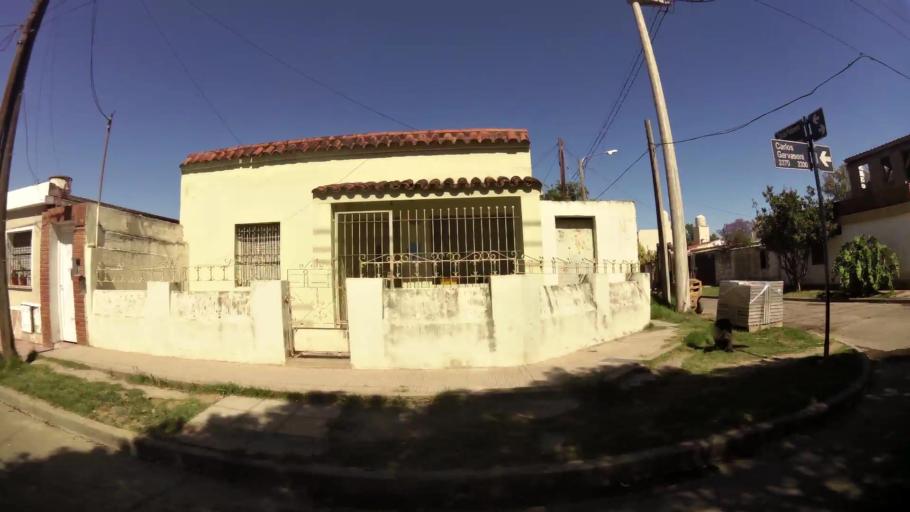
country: AR
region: Cordoba
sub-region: Departamento de Capital
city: Cordoba
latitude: -31.4363
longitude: -64.1356
